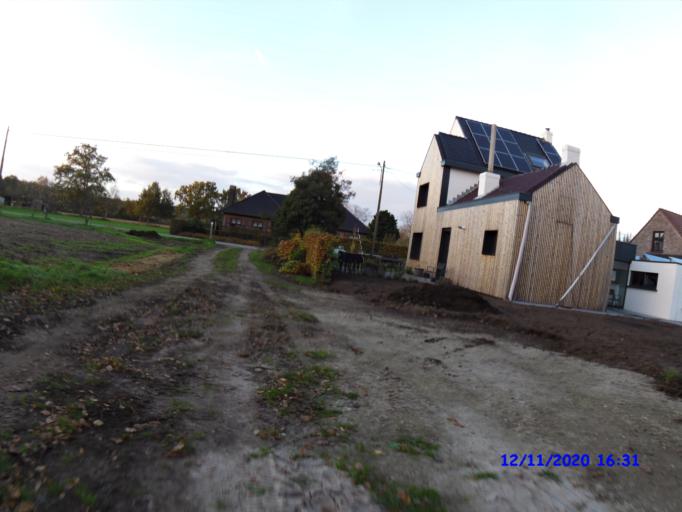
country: BE
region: Flanders
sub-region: Provincie Antwerpen
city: Meerhout
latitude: 51.1869
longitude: 5.0521
